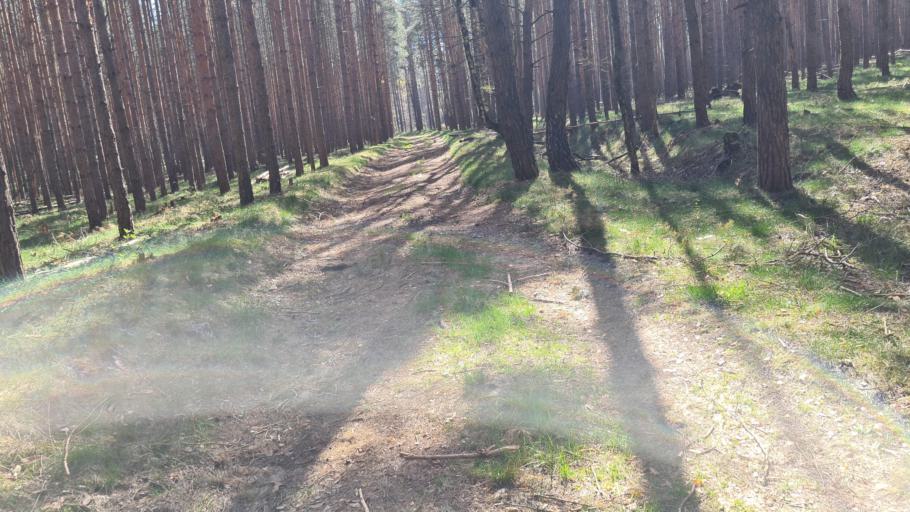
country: DE
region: Brandenburg
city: Groden
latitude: 51.3896
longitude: 13.5703
